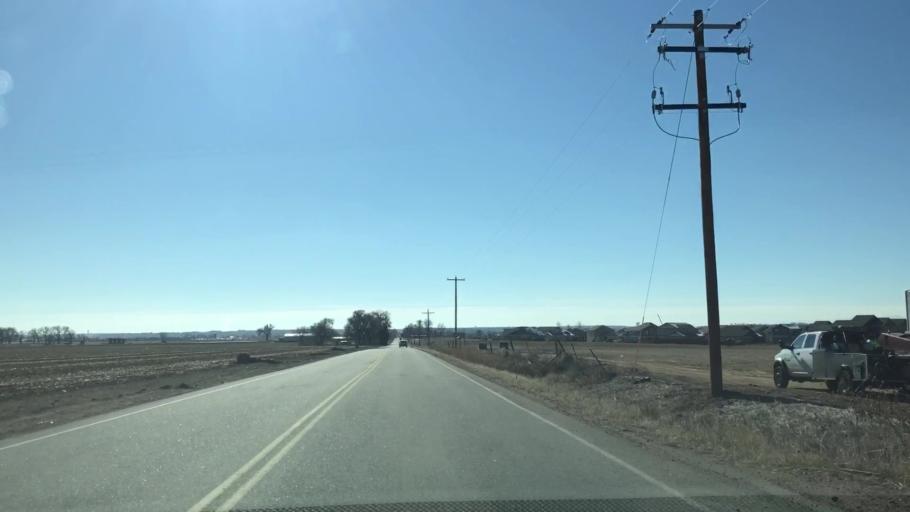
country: US
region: Colorado
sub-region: Weld County
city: Windsor
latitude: 40.5173
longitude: -104.9443
